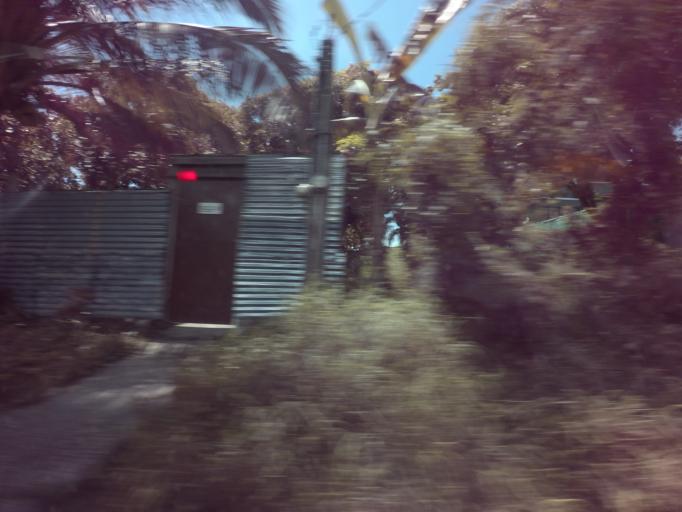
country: PH
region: Calabarzon
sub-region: Province of Rizal
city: Las Pinas
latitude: 14.4216
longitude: 120.9954
